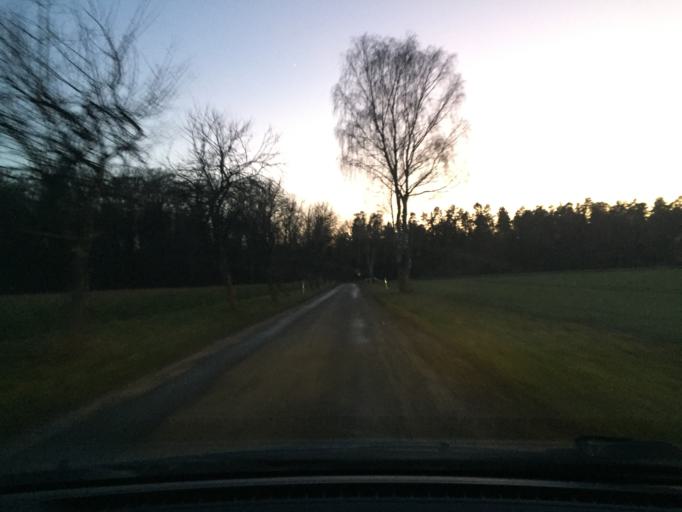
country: DE
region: Lower Saxony
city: Gohrde
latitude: 53.1776
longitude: 10.9205
